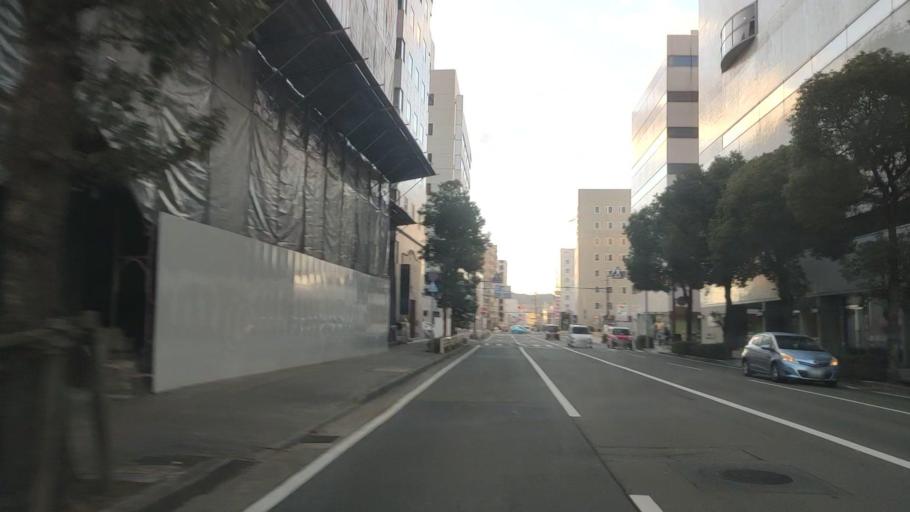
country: JP
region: Hyogo
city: Himeji
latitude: 34.8250
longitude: 134.6904
